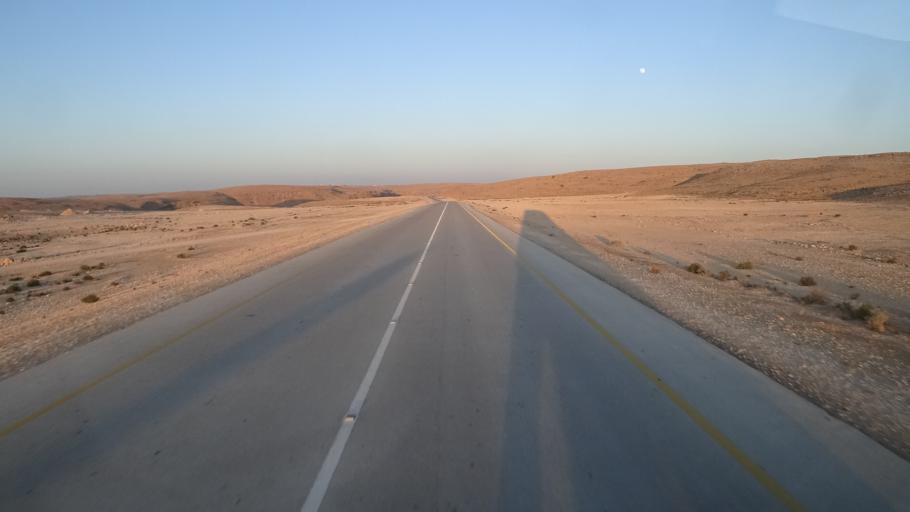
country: YE
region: Al Mahrah
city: Hawf
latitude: 16.9508
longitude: 53.3221
